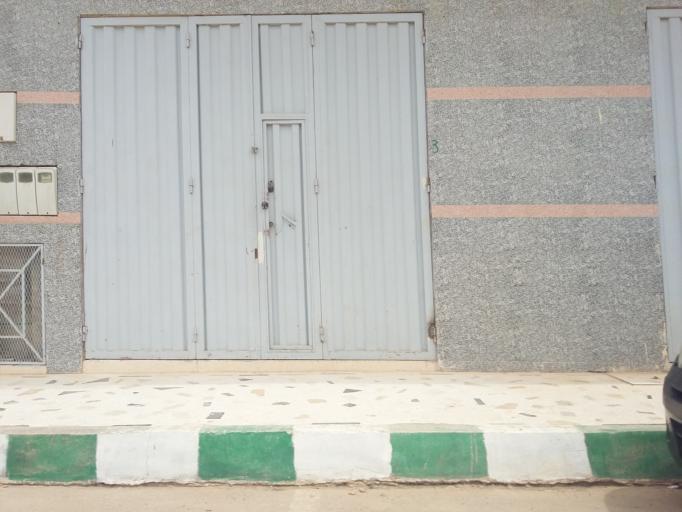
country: MA
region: Fes-Boulemane
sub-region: Fes
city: Fes
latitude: 34.0005
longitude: -5.0082
